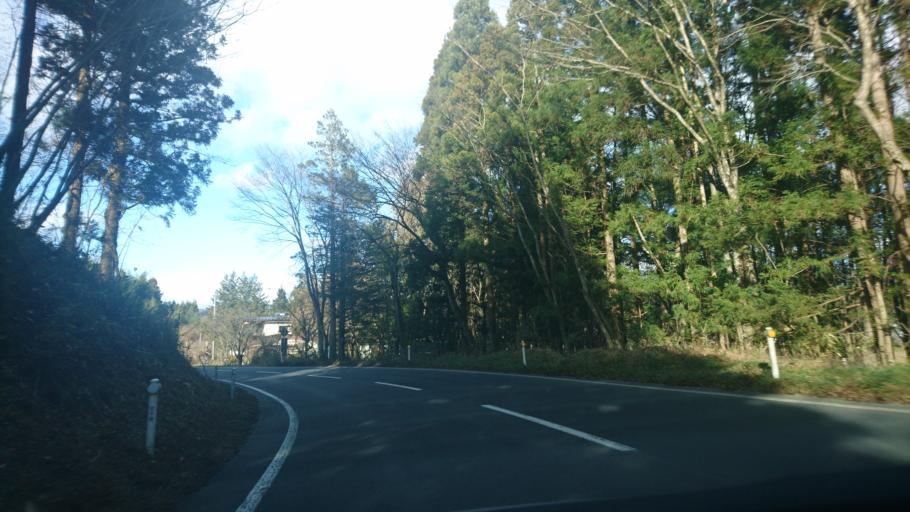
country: JP
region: Iwate
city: Ichinoseki
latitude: 38.9437
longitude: 141.4076
